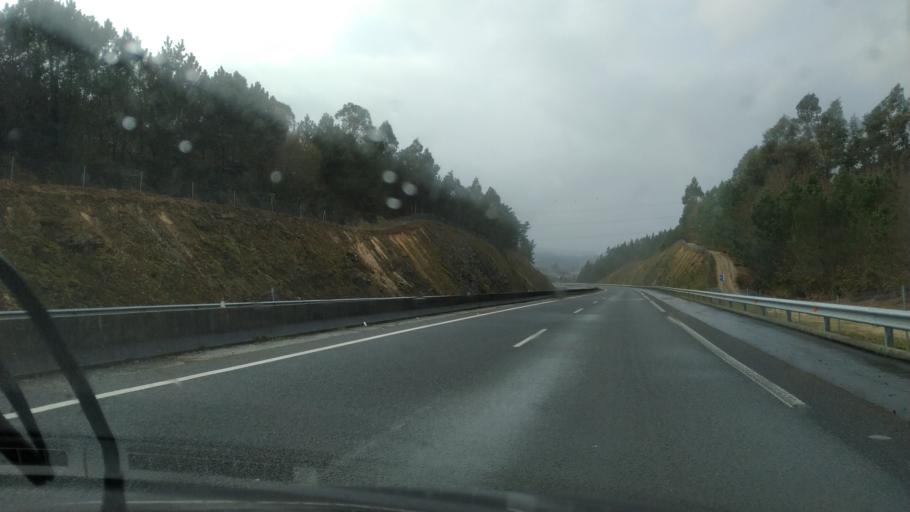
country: ES
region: Galicia
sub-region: Provincia de Pontevedra
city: Silleda
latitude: 42.7190
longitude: -8.2722
